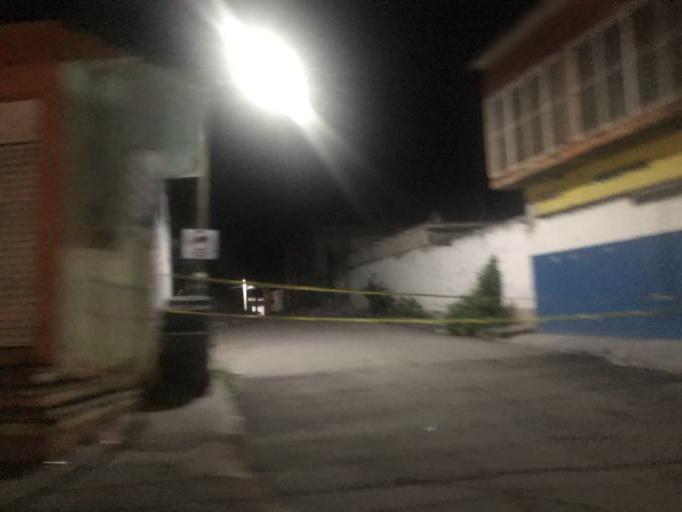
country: MX
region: Morelos
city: Tlaquiltenango
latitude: 18.6405
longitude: -99.1583
